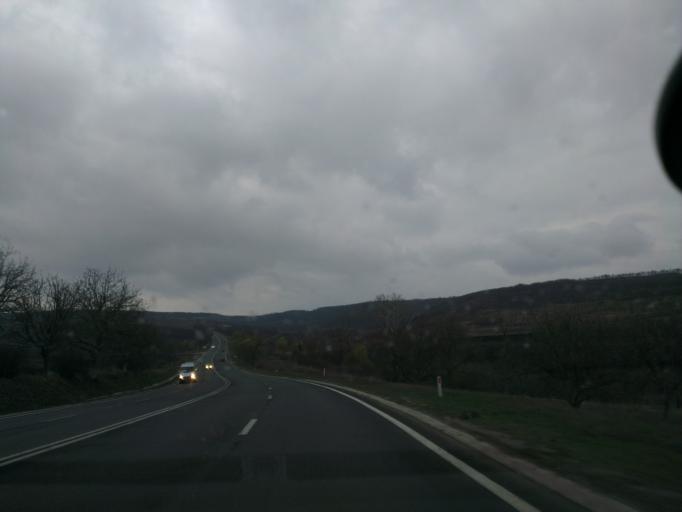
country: MD
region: Laloveni
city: Ialoveni
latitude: 46.9256
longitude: 28.6966
